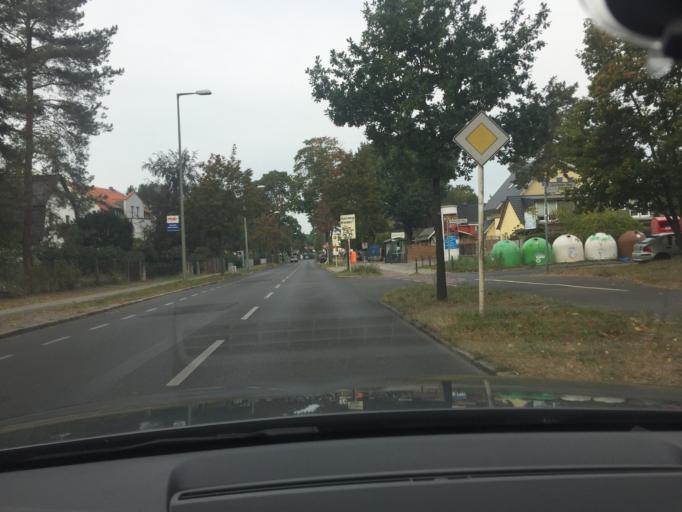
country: DE
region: Berlin
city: Rahnsdorf
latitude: 52.4357
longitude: 13.6999
